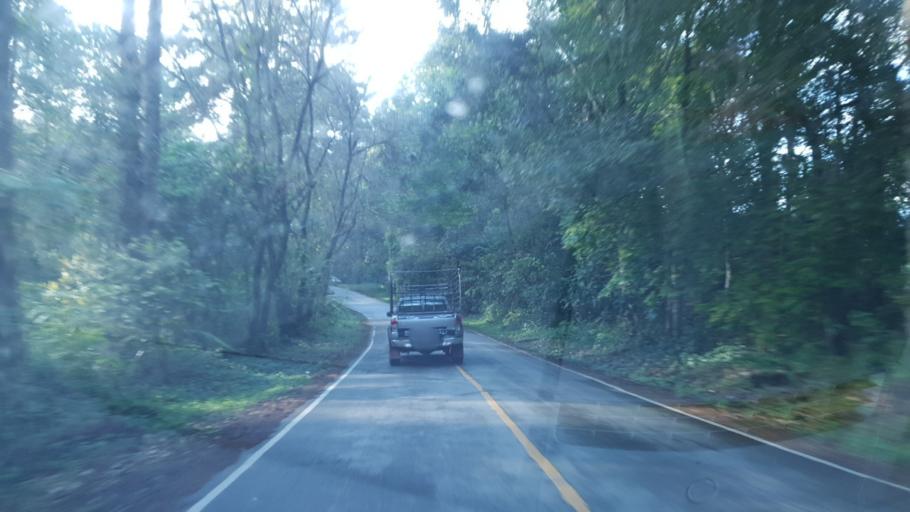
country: TH
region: Chiang Mai
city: Mae Chaem
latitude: 18.5135
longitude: 98.4708
